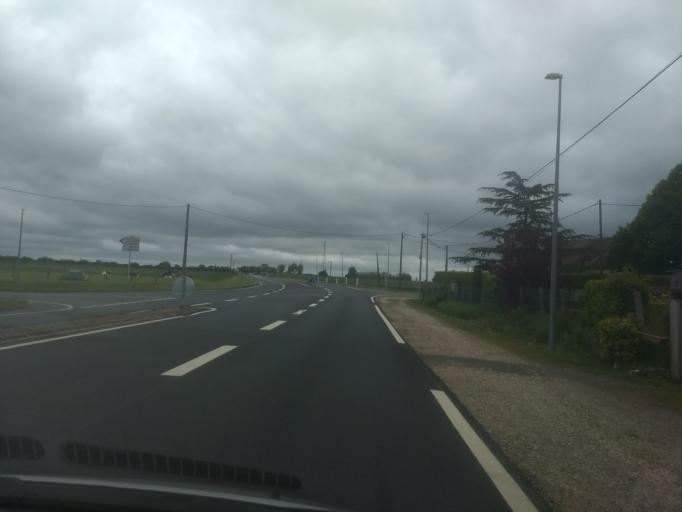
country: FR
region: Centre
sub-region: Departement d'Eure-et-Loir
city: Chateauneuf-en-Thymerais
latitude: 48.5675
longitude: 1.2203
